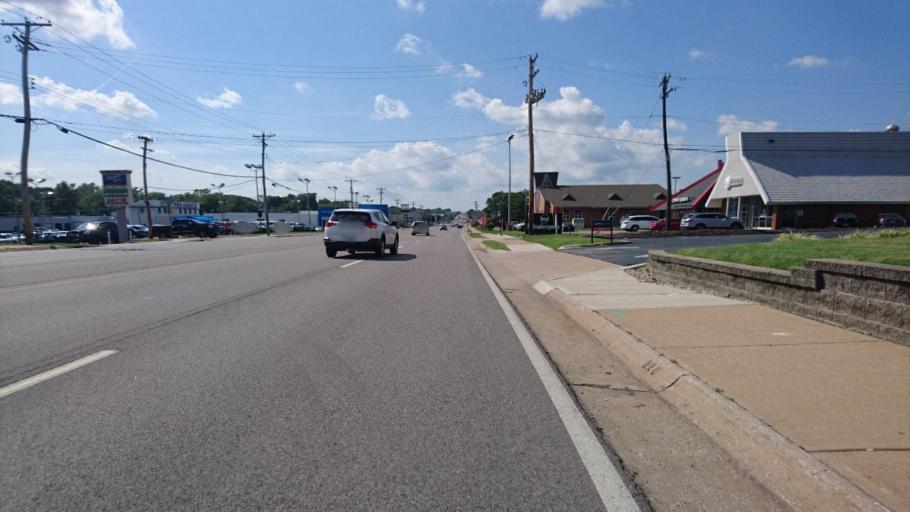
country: US
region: Missouri
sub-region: Saint Louis County
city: Ballwin
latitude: 38.5930
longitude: -90.5487
